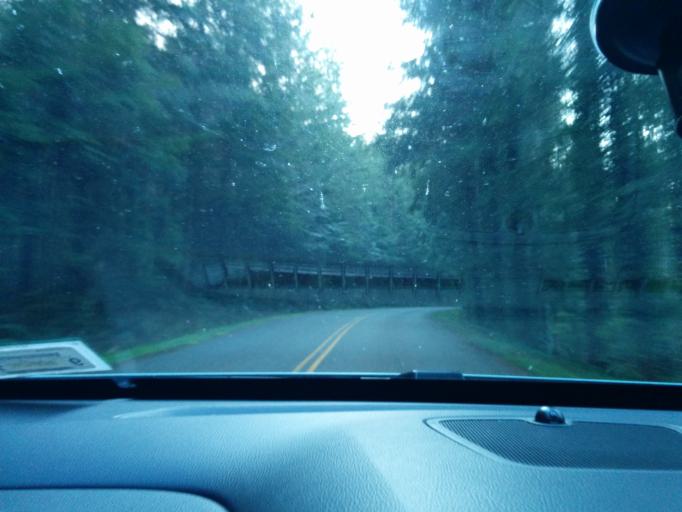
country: US
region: Washington
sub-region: Snohomish County
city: Sultan
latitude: 47.8983
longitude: -121.7587
